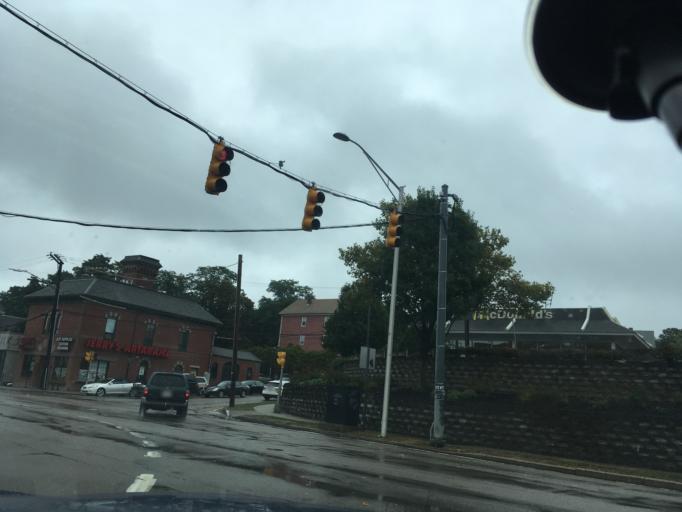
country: US
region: Rhode Island
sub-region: Providence County
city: Providence
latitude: 41.8380
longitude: -71.4095
